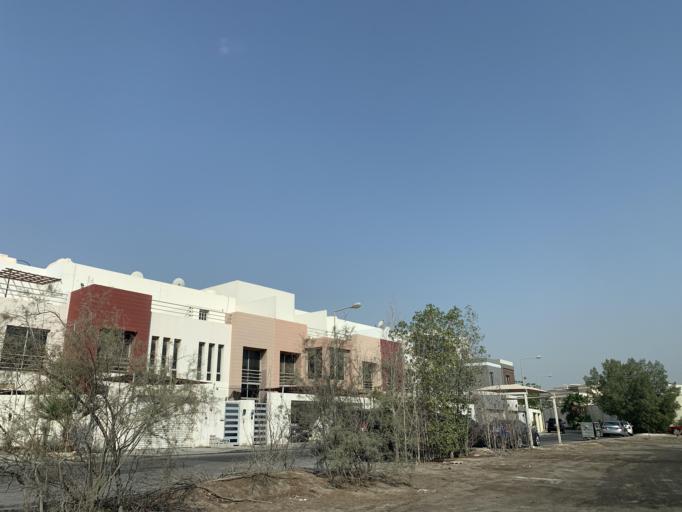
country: BH
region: Northern
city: Madinat `Isa
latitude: 26.1943
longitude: 50.5153
